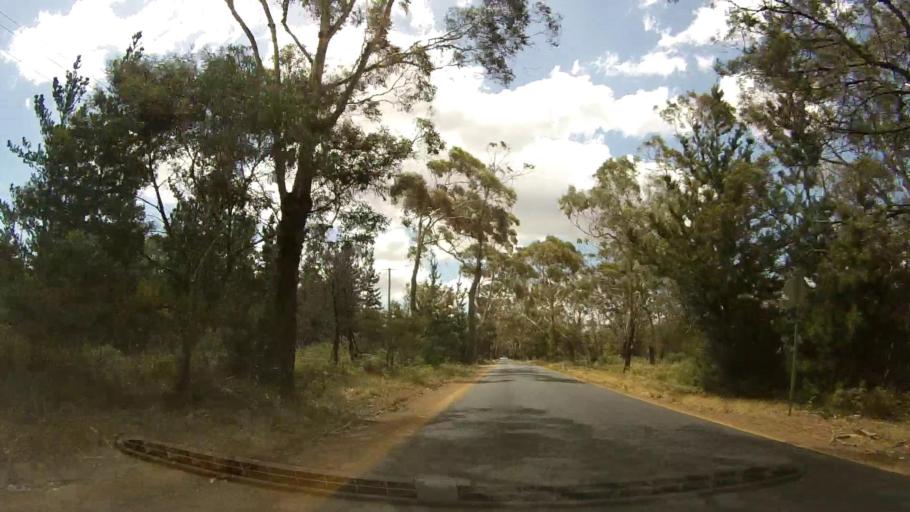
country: AU
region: Tasmania
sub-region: Clarence
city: Seven Mile Beach
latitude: -42.8265
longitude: 147.5072
